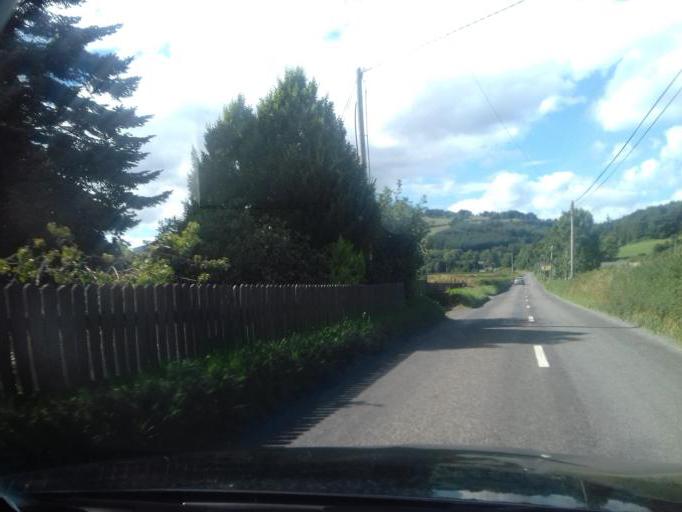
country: IE
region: Munster
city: Carrick-on-Suir
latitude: 52.3986
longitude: -7.4762
